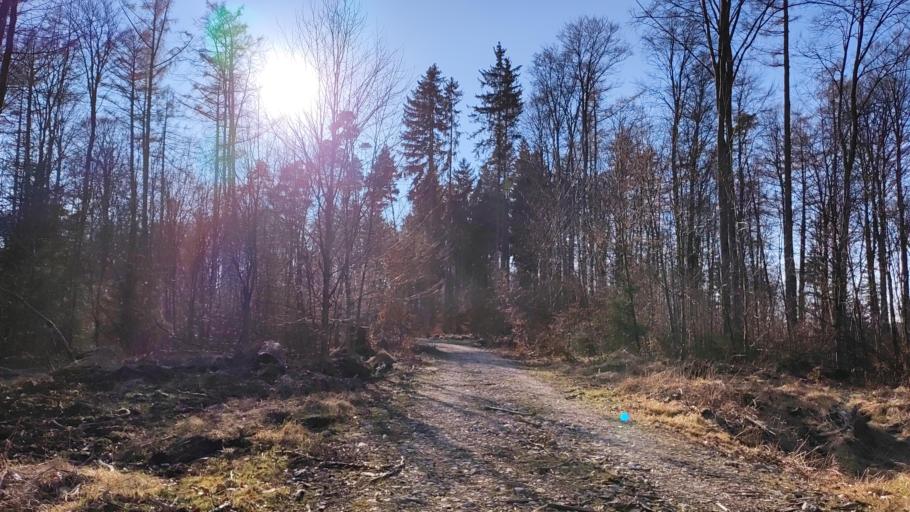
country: DE
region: Bavaria
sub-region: Swabia
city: Zusmarshausen
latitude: 48.4275
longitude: 10.6147
